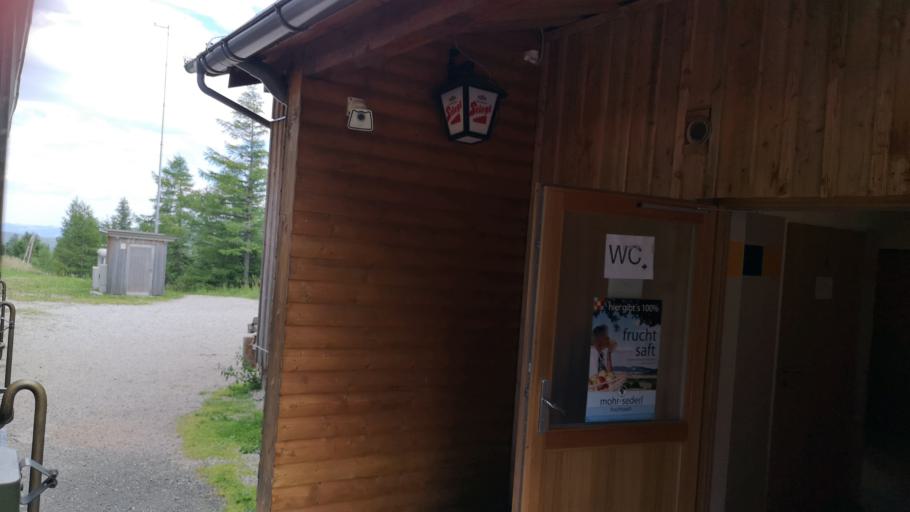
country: AT
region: Lower Austria
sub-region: Politischer Bezirk Neunkirchen
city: Reichenau an der Rax
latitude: 47.7534
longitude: 15.8509
